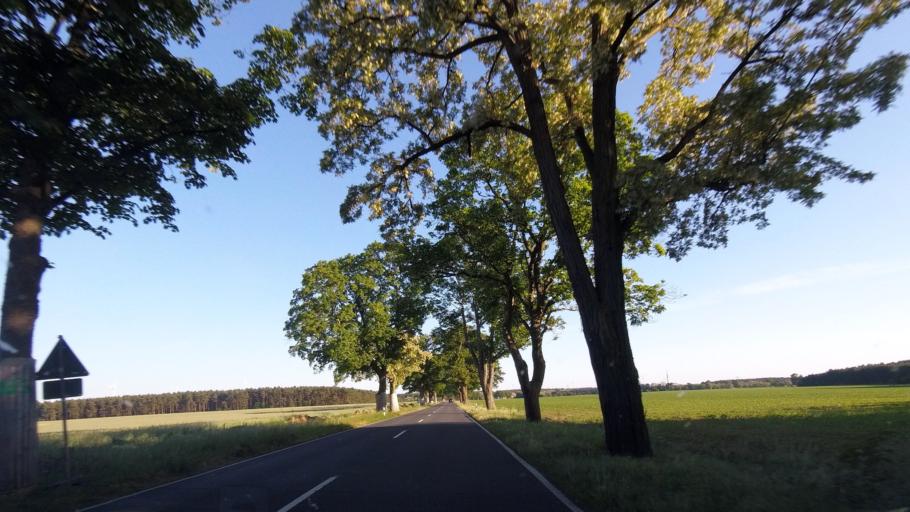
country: DE
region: Brandenburg
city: Golzow
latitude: 52.3446
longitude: 12.6010
